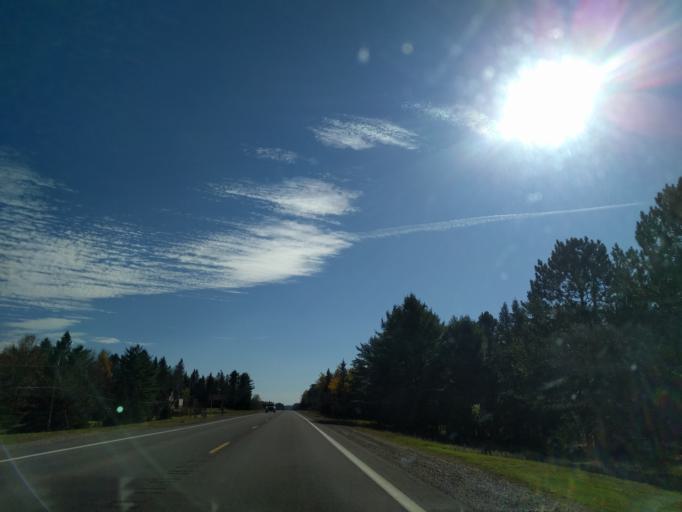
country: US
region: Michigan
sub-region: Marquette County
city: West Ishpeming
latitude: 46.3896
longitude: -87.9960
